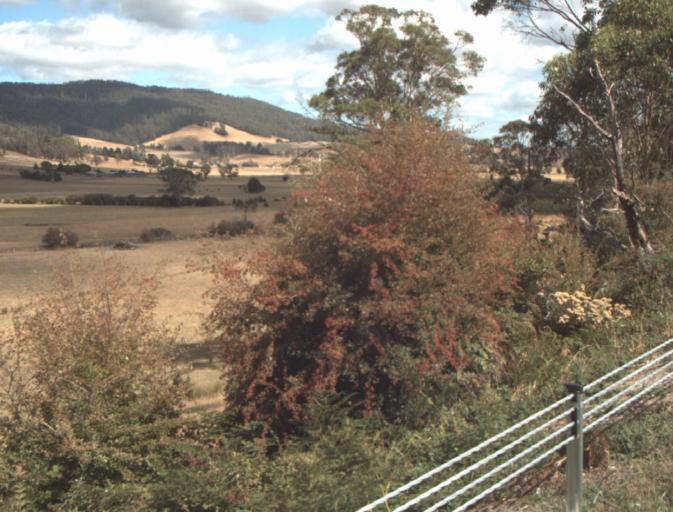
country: AU
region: Tasmania
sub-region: Launceston
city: Mayfield
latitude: -41.2407
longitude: 147.1490
